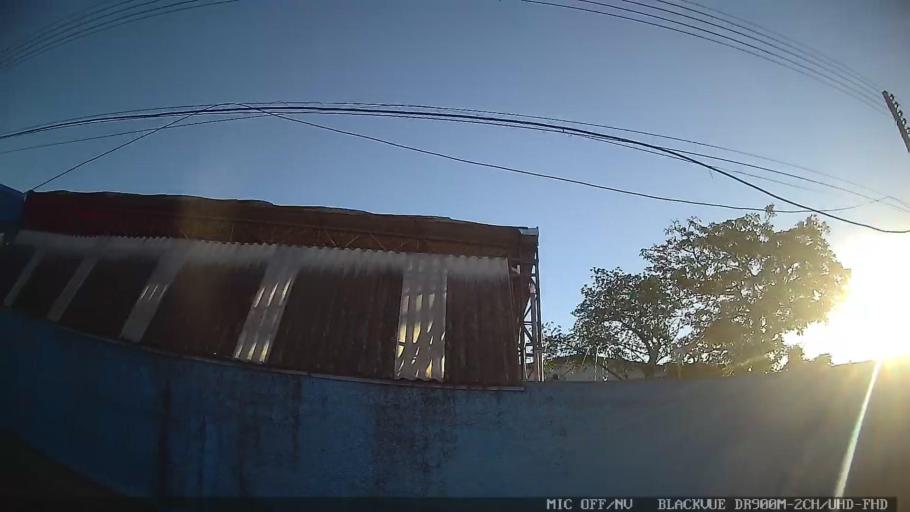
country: BR
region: Sao Paulo
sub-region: Guaruja
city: Guaruja
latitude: -23.9668
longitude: -46.2738
